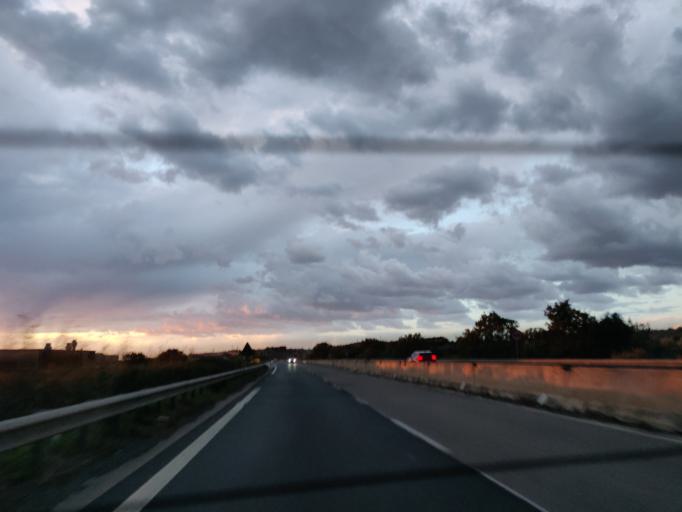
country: IT
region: Tuscany
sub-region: Provincia di Livorno
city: San Vincenzo
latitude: 43.0827
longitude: 10.5566
